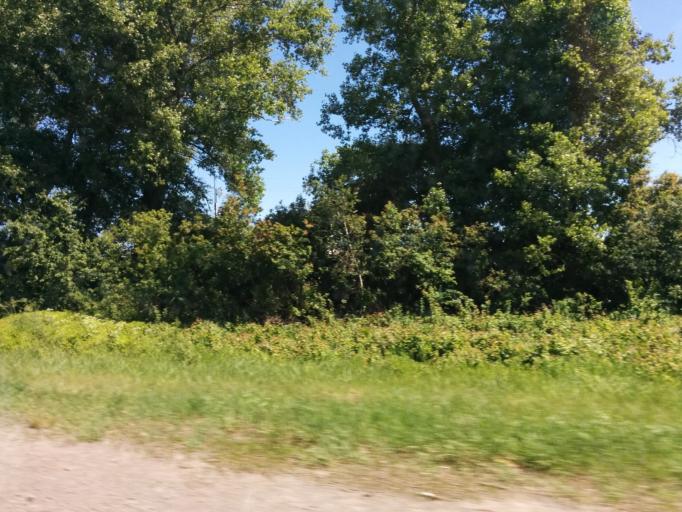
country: RU
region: Tambov
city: Sosnovka
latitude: 53.1393
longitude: 41.5524
